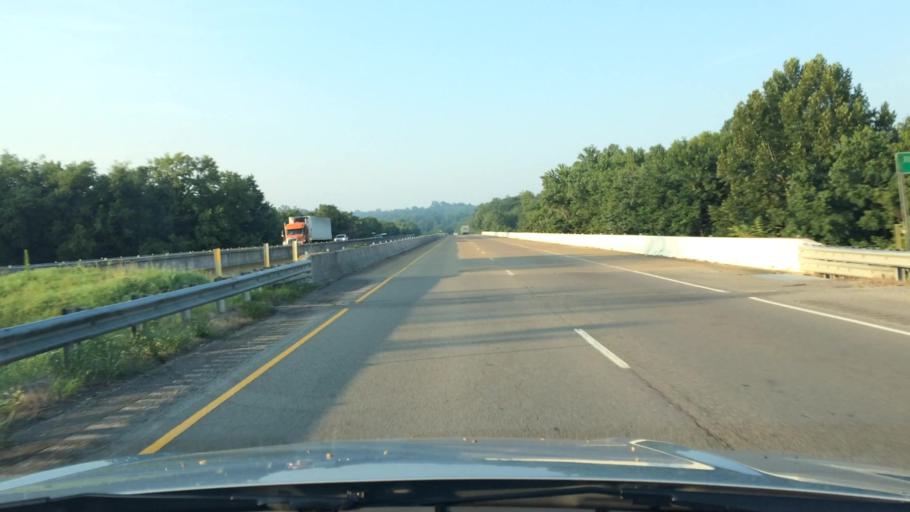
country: US
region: Tennessee
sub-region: Giles County
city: Pulaski
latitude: 35.1967
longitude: -87.0639
